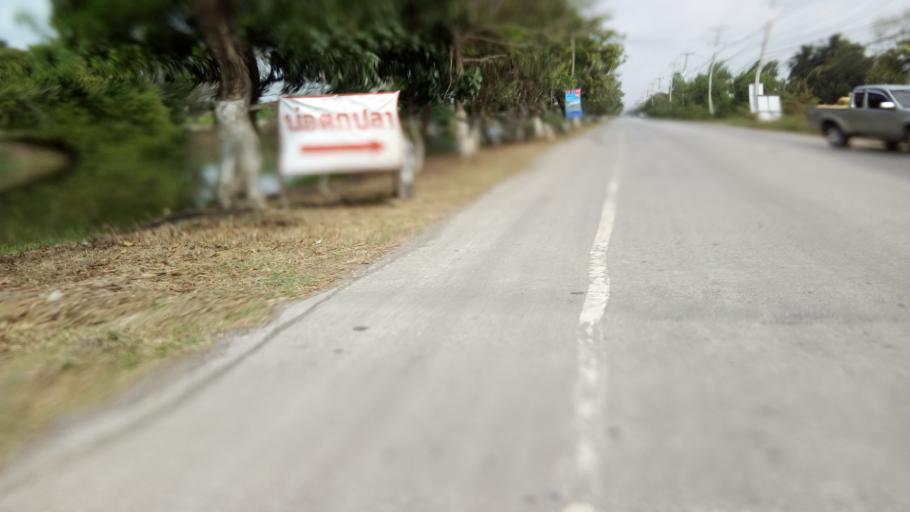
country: TH
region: Pathum Thani
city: Nong Suea
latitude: 14.1480
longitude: 100.8238
